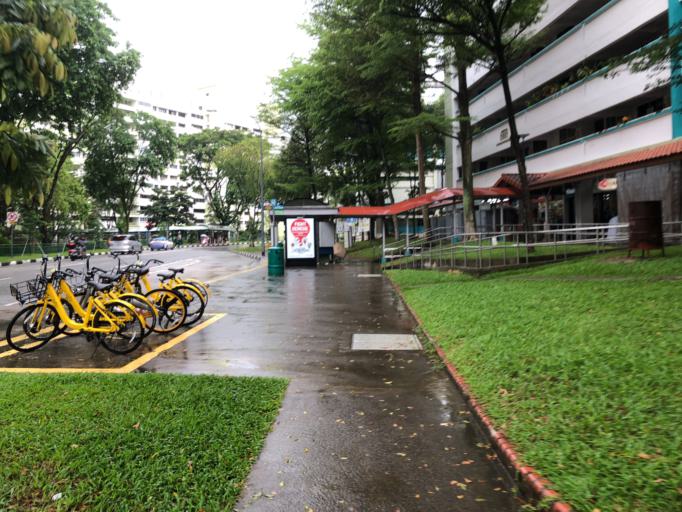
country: SG
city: Singapore
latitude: 1.3486
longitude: 103.7574
